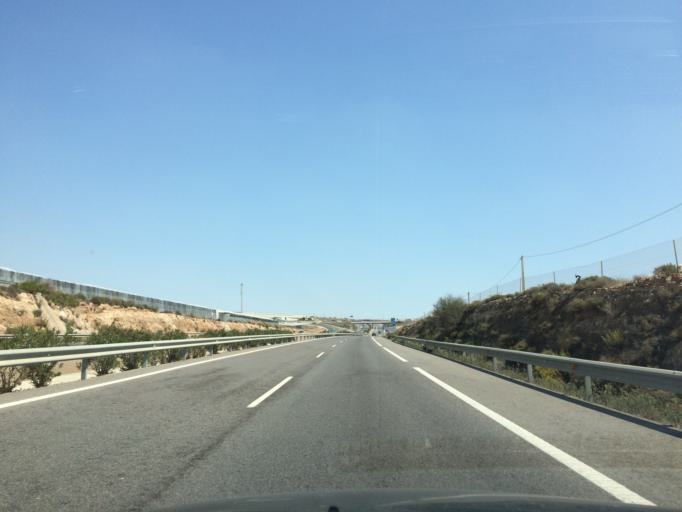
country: ES
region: Andalusia
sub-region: Provincia de Almeria
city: Dalias
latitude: 36.7582
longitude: -2.9234
